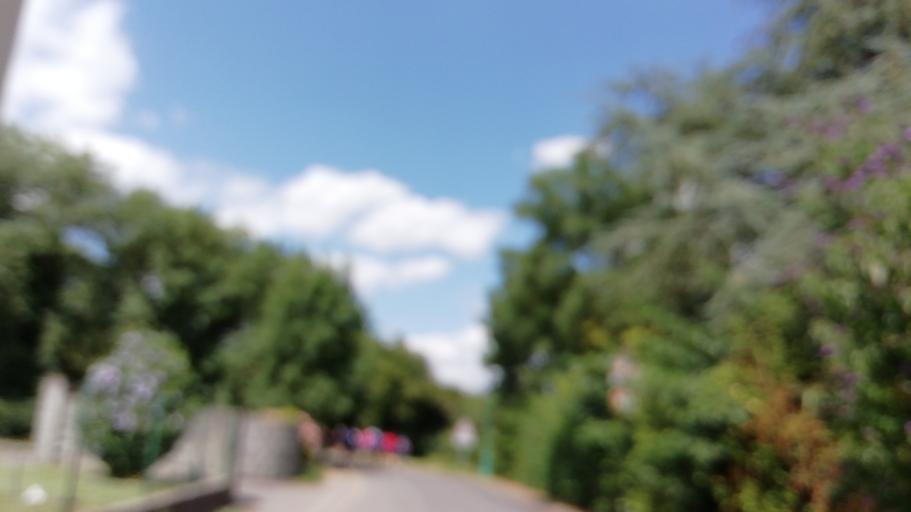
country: FR
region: Poitou-Charentes
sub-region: Departement de la Vienne
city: Thure
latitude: 46.8332
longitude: 0.4573
